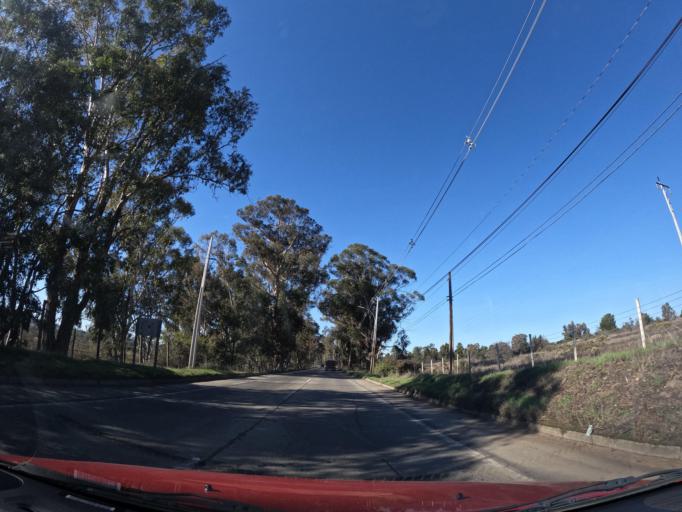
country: CL
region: Maule
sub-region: Provincia de Cauquenes
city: Cauquenes
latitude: -35.9579
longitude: -72.2914
